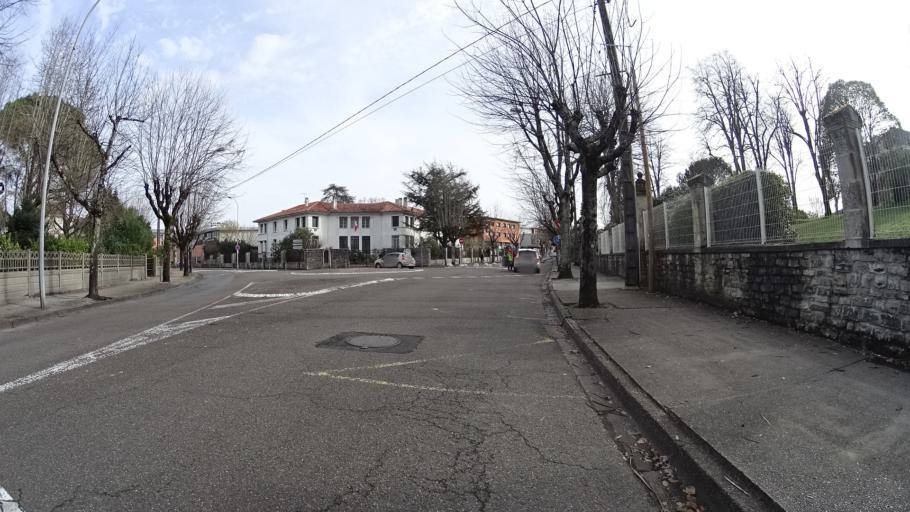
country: FR
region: Aquitaine
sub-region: Departement des Landes
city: Dax
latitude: 43.7040
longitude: -1.0571
